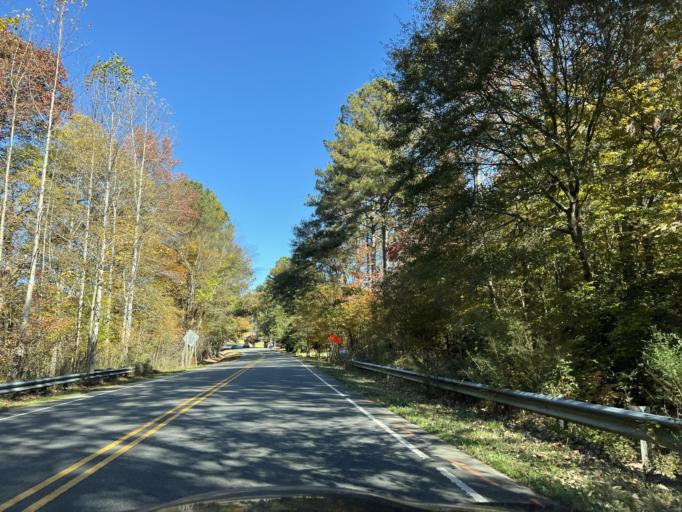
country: US
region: North Carolina
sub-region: Wake County
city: Fuquay-Varina
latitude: 35.6360
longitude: -78.7275
